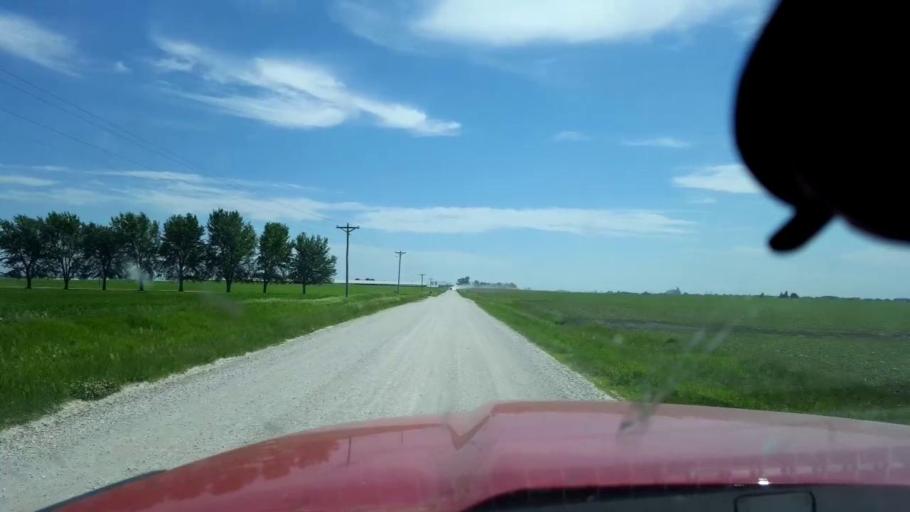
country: US
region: Iowa
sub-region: Hamilton County
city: Jewell
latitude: 42.3505
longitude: -93.5604
